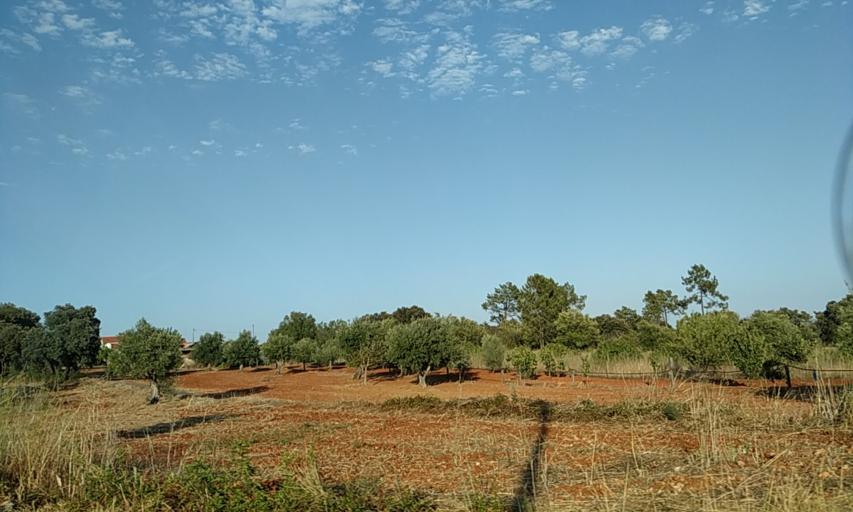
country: PT
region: Santarem
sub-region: Alcanena
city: Alcanena
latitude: 39.4435
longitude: -8.6241
